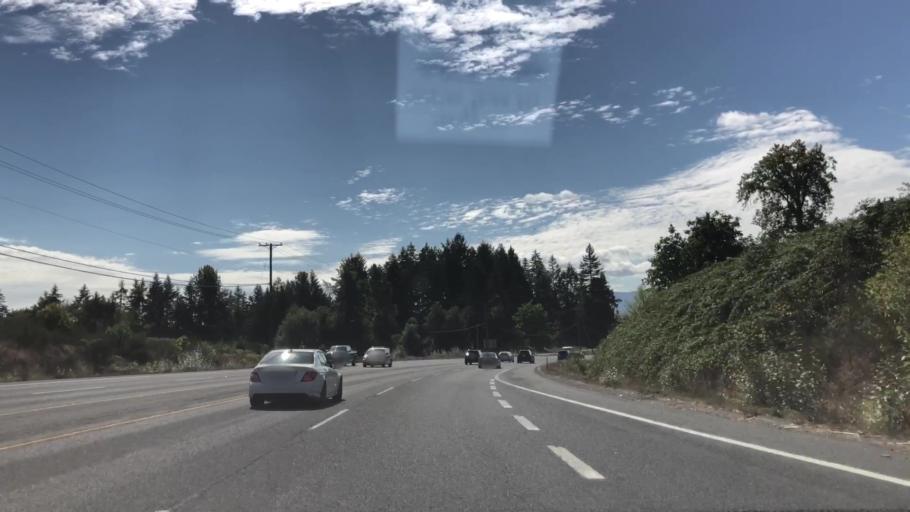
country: CA
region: British Columbia
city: Nanaimo
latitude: 49.1213
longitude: -123.8629
